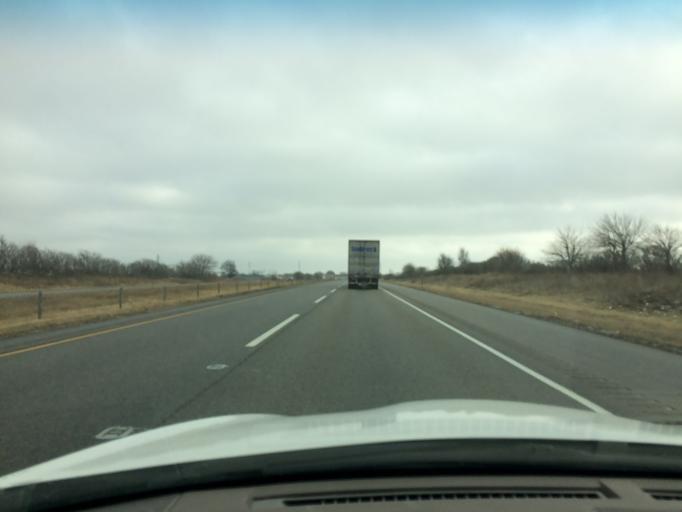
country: US
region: Illinois
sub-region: Kane County
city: Maple Park
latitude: 41.8849
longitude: -88.6265
